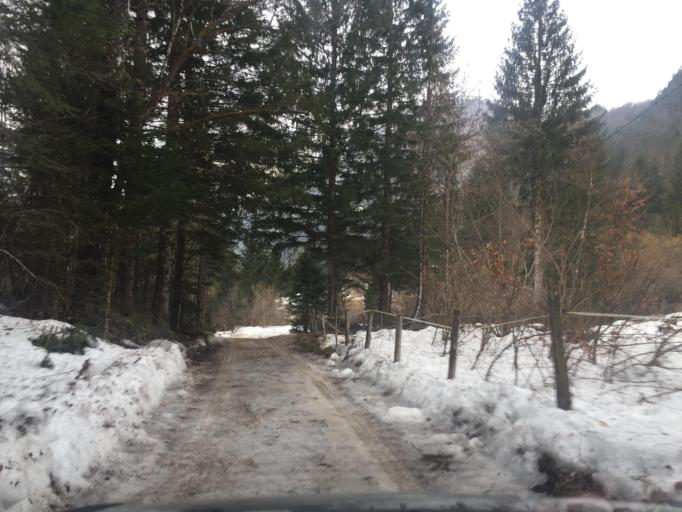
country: IT
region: Friuli Venezia Giulia
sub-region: Provincia di Udine
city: Tarvisio
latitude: 46.4122
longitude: 13.6201
